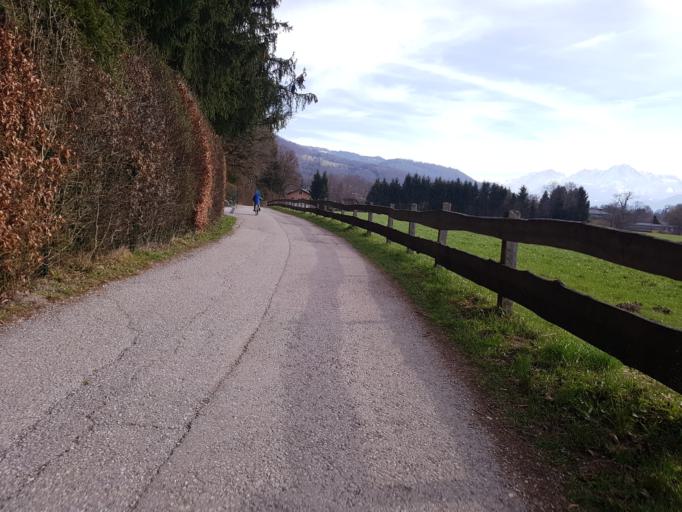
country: AT
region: Salzburg
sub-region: Salzburg Stadt
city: Salzburg
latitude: 47.7937
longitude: 13.0852
